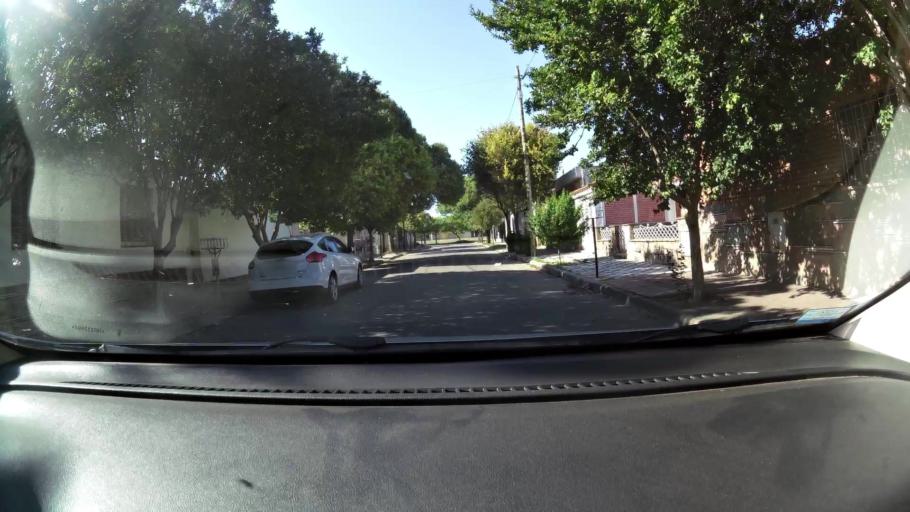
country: AR
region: Cordoba
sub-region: Departamento de Capital
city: Cordoba
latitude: -31.3927
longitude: -64.1456
